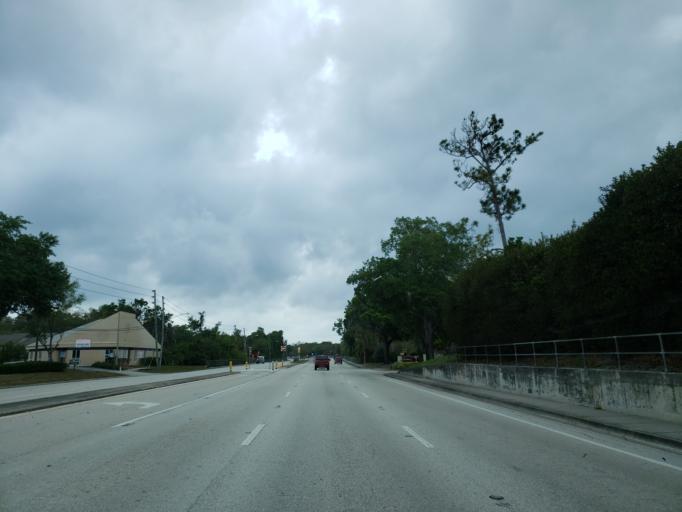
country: US
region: Florida
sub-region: Pinellas County
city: Saint George
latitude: 28.0641
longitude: -82.7144
